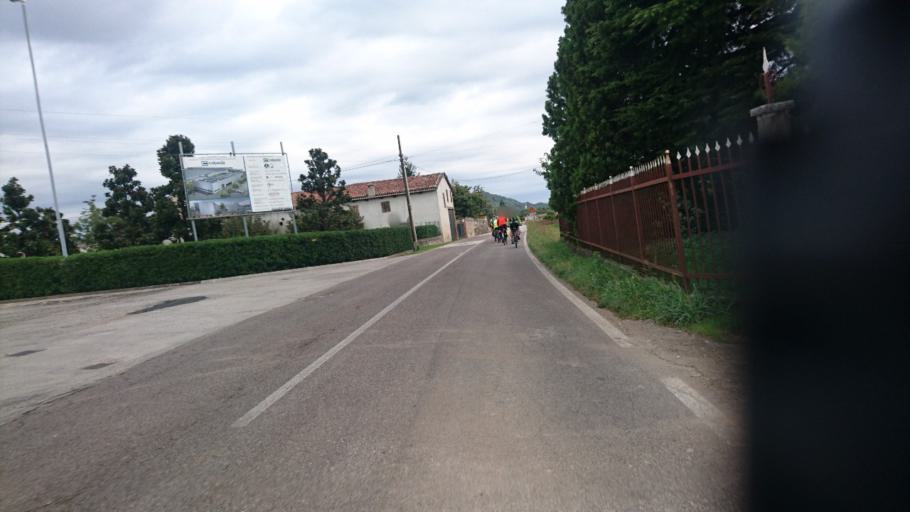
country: IT
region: Veneto
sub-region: Provincia di Vicenza
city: Montorso Vicentino
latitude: 45.4958
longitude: 11.3789
